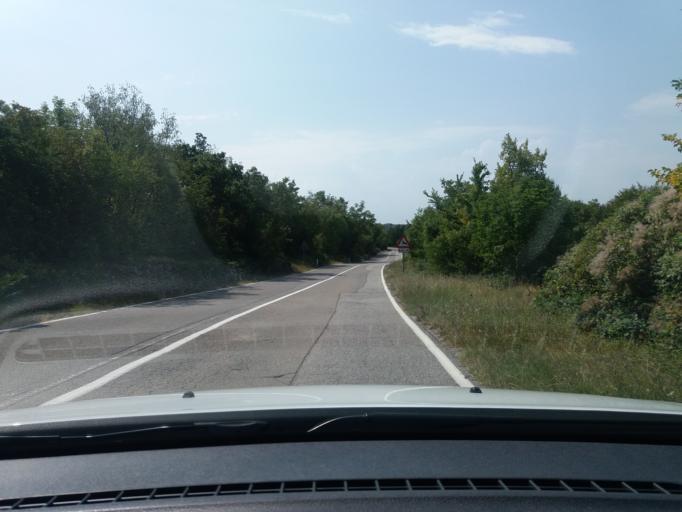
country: SI
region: Miren-Kostanjevica
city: Miren
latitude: 45.8637
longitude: 13.5868
